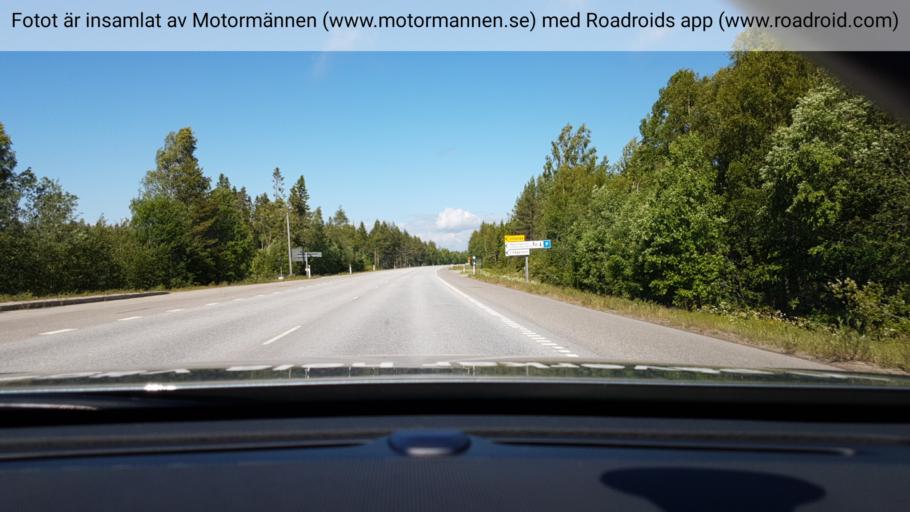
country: SE
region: Vaesterbotten
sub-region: Umea Kommun
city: Holmsund
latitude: 63.7539
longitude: 20.3598
